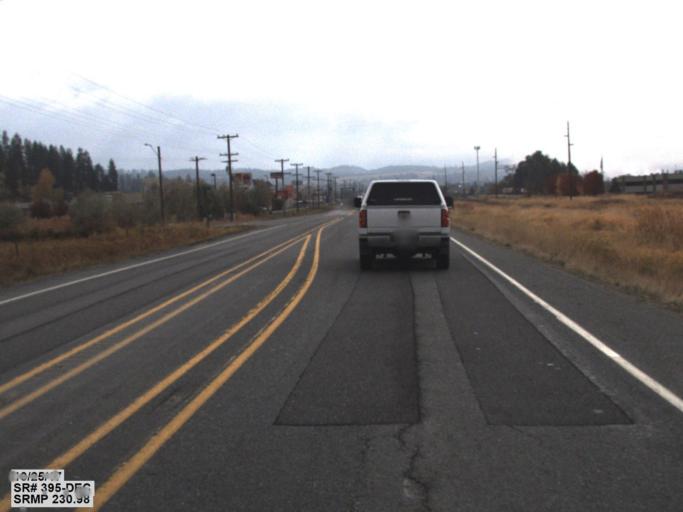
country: US
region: Washington
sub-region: Stevens County
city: Colville
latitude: 48.5588
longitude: -117.9266
